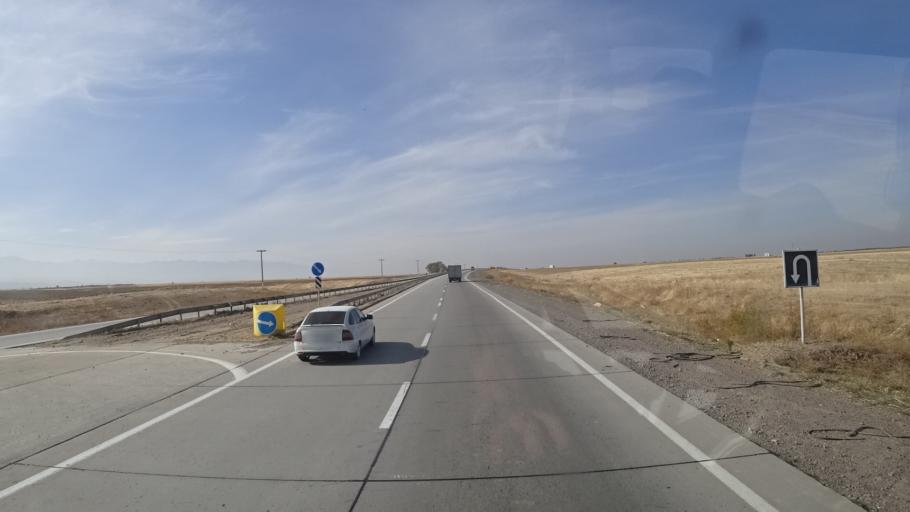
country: KZ
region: Zhambyl
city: Merke
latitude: 42.8900
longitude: 72.9790
